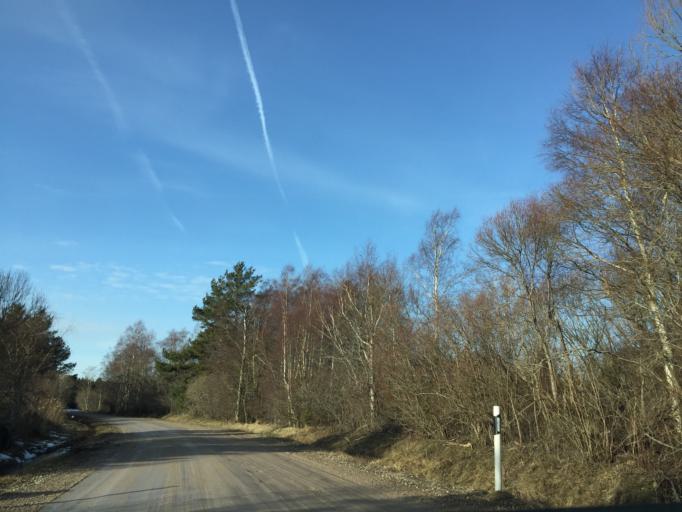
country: EE
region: Saare
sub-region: Kuressaare linn
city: Kuressaare
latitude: 58.3672
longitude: 22.0291
